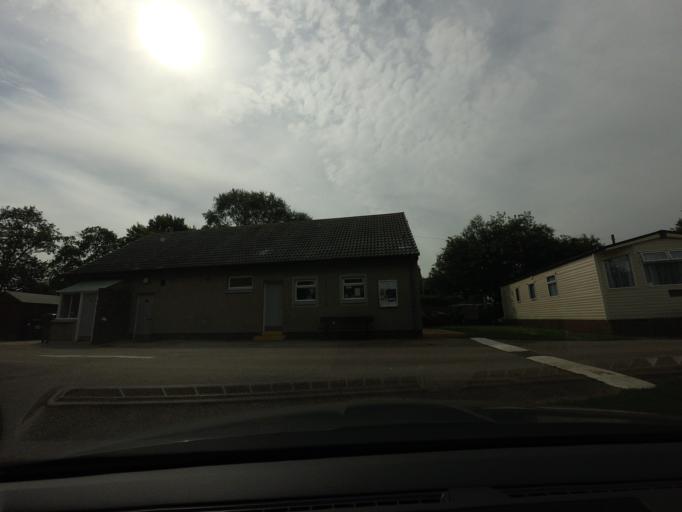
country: GB
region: Scotland
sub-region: Aberdeenshire
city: Turriff
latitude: 57.5333
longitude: -2.4591
